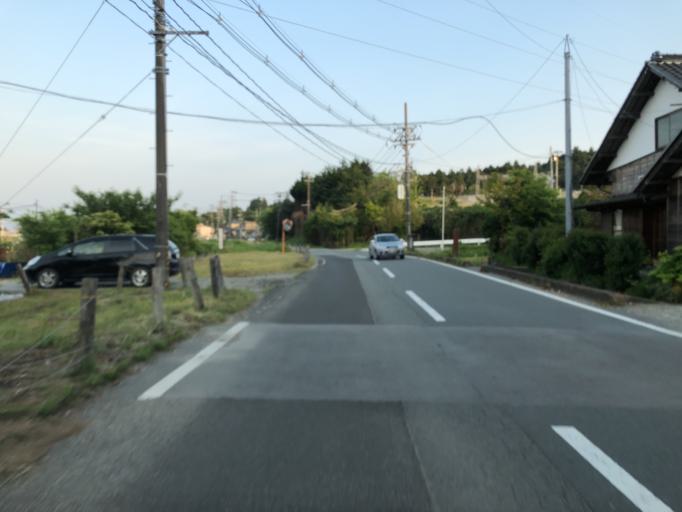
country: JP
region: Fukushima
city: Namie
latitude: 37.2694
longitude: 140.9914
